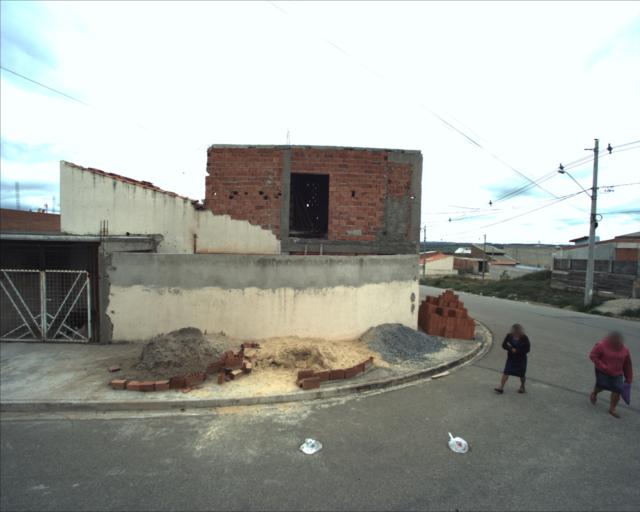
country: BR
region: Sao Paulo
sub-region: Sorocaba
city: Sorocaba
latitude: -23.4391
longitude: -47.5004
